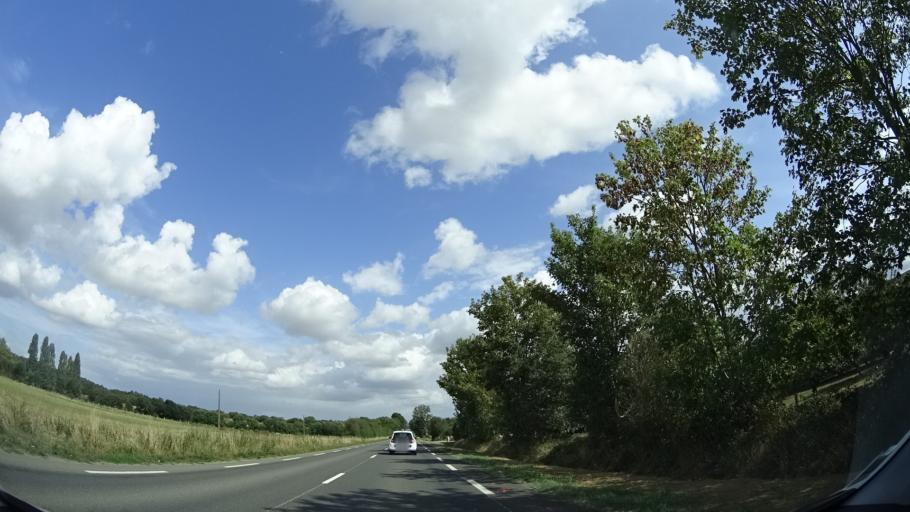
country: FR
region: Pays de la Loire
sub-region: Departement de la Sarthe
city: Louplande
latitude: 48.0202
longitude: -0.0658
